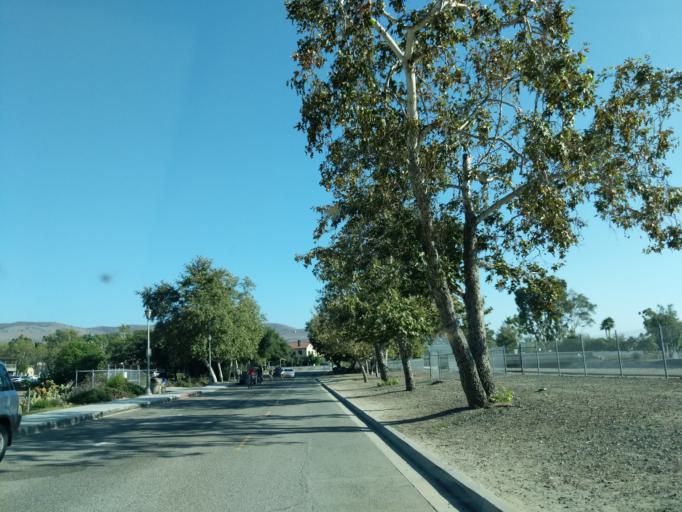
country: US
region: California
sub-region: Orange County
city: San Juan Capistrano
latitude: 33.4995
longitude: -117.6657
